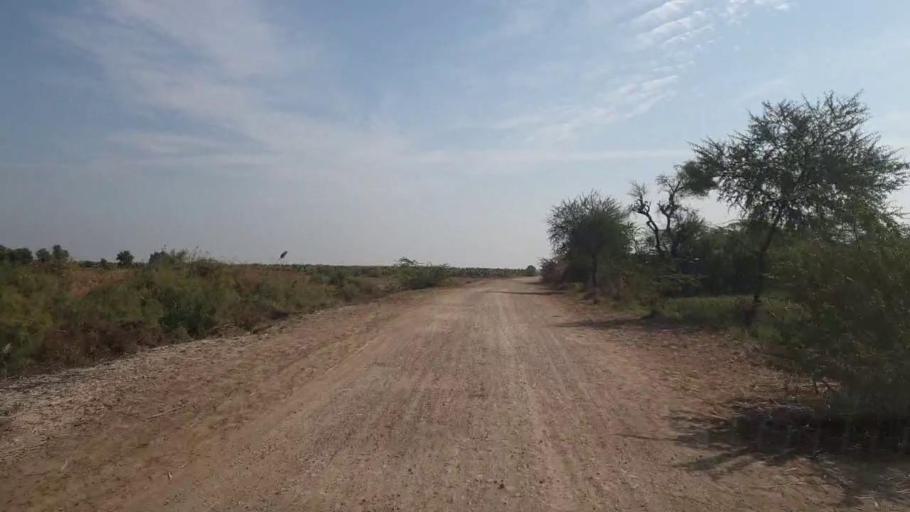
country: PK
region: Sindh
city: Mirwah Gorchani
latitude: 25.3748
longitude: 69.2006
